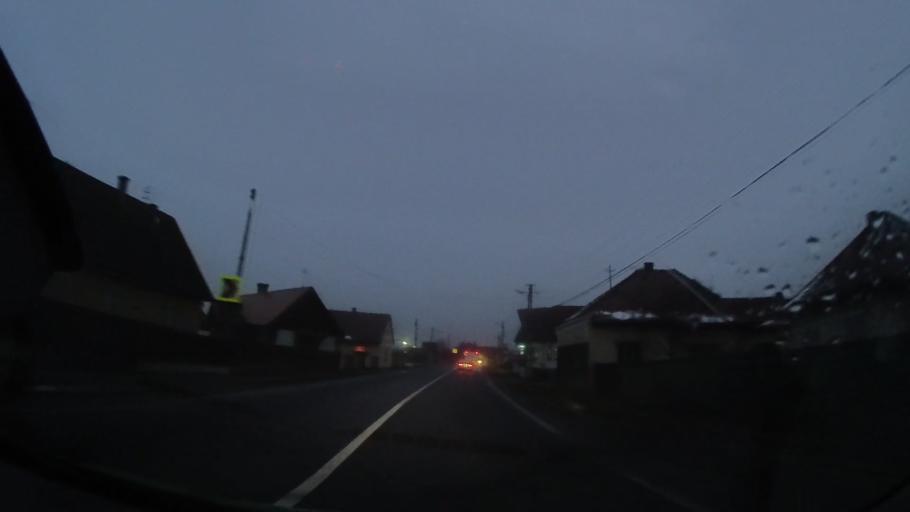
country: RO
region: Harghita
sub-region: Comuna Ditrau
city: Ditrau
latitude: 46.8062
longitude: 25.4934
